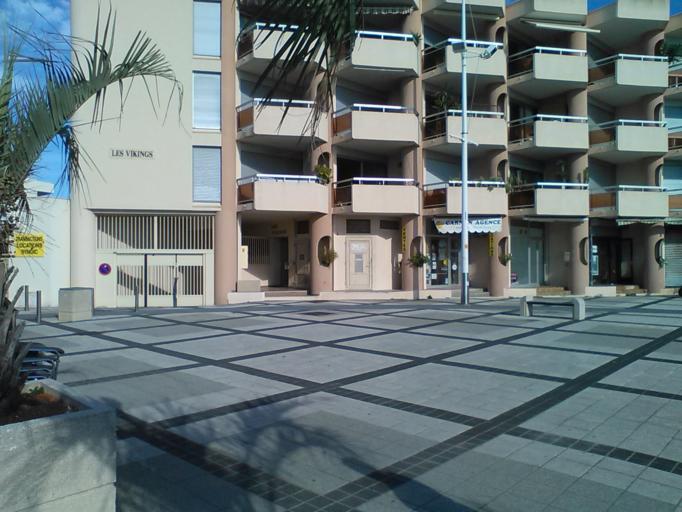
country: FR
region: Languedoc-Roussillon
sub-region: Departement de l'Herault
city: Perols
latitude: 43.5431
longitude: 3.9751
